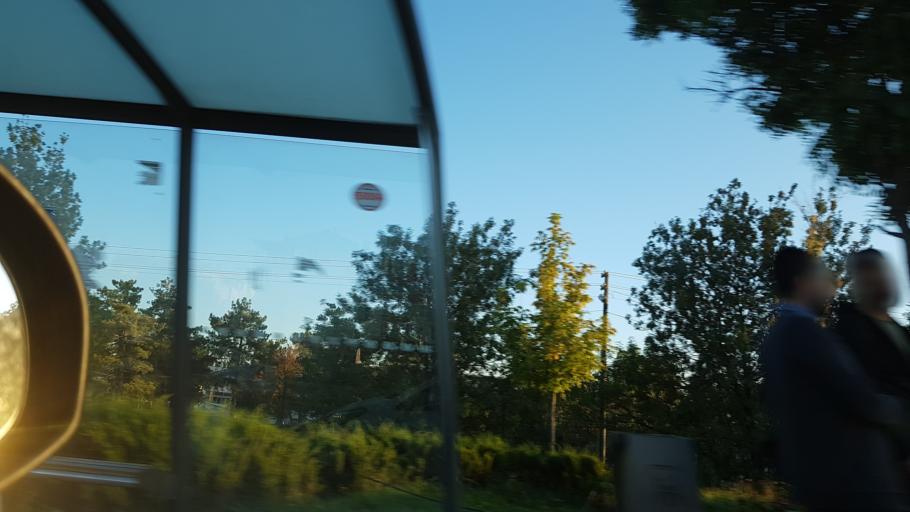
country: TR
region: Ankara
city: Etimesgut
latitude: 39.9627
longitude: 32.6631
